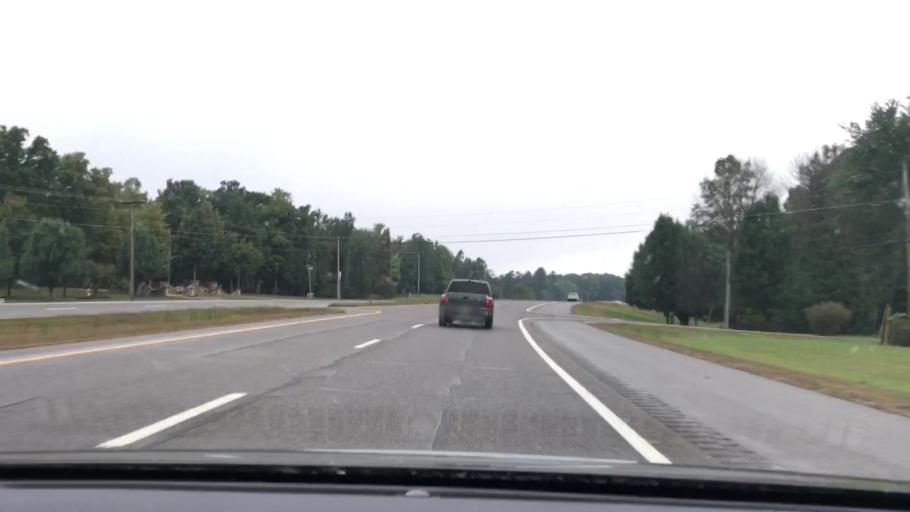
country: US
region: Tennessee
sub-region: Fentress County
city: Jamestown
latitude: 36.3744
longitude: -84.9440
